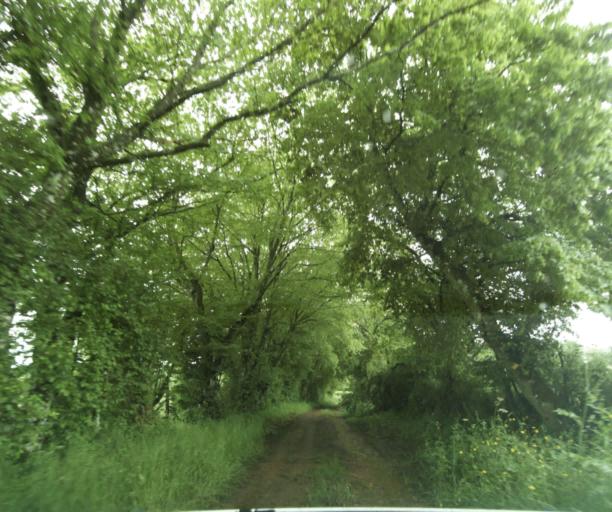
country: FR
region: Bourgogne
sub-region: Departement de Saone-et-Loire
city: Charolles
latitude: 46.4621
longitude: 4.3529
